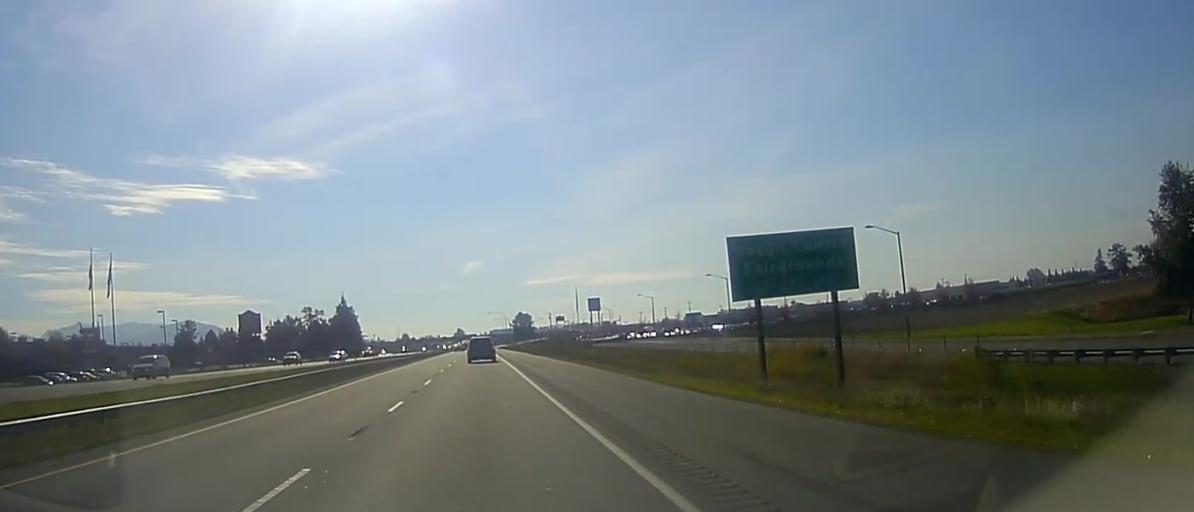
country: US
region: Washington
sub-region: Skagit County
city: Burlington
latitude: 48.4578
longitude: -122.3417
